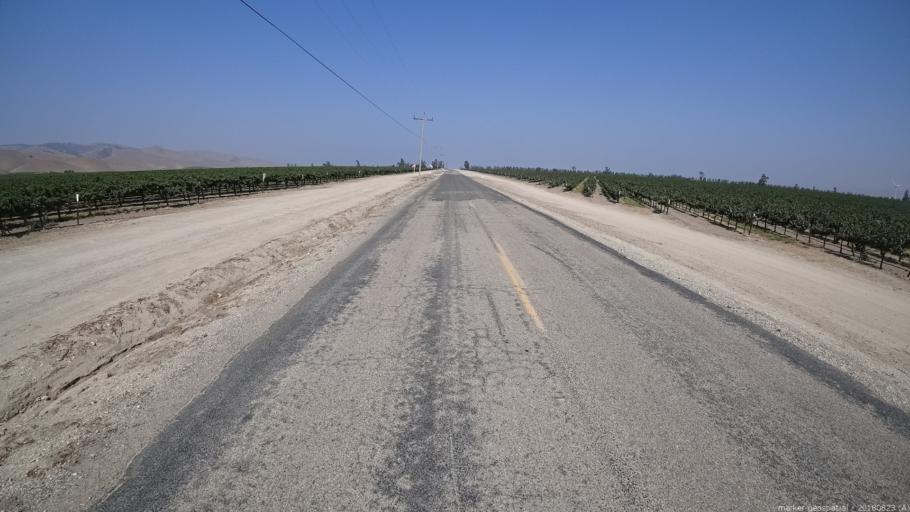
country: US
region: California
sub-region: Monterey County
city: Greenfield
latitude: 36.2531
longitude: -121.1994
